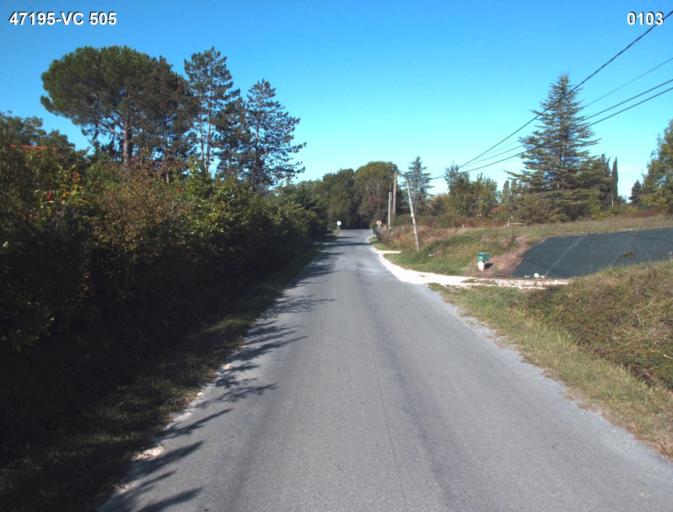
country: FR
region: Aquitaine
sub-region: Departement du Lot-et-Garonne
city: Nerac
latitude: 44.1407
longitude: 0.3629
